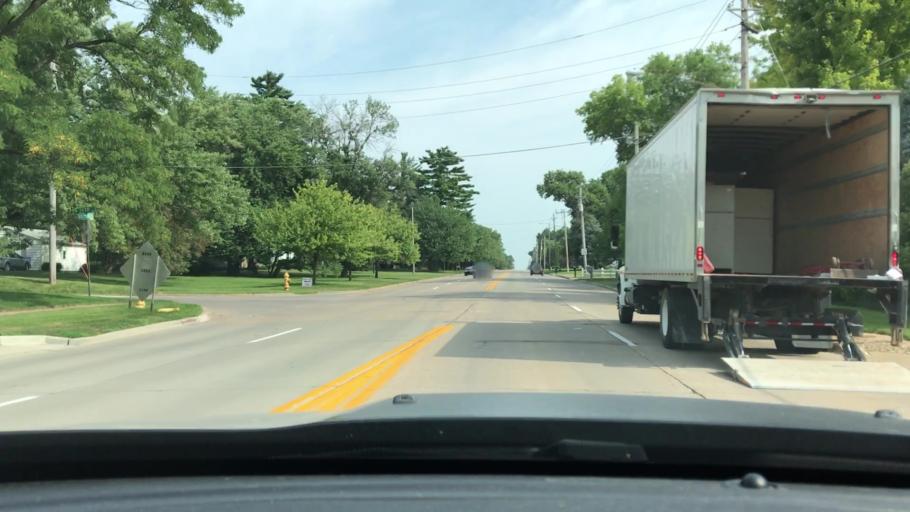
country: US
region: Iowa
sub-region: Scott County
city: Bettendorf
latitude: 41.5586
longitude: -90.5417
